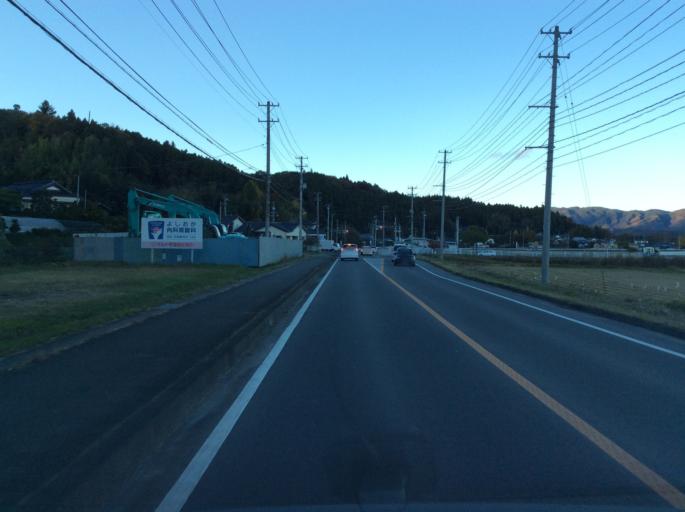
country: JP
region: Fukushima
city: Iwaki
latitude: 37.0688
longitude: 140.8714
